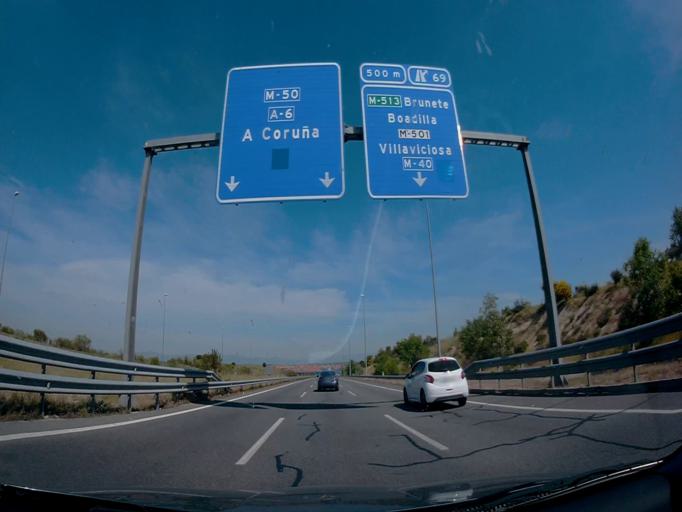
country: ES
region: Madrid
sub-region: Provincia de Madrid
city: Boadilla del Monte
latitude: 40.3849
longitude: -3.8800
